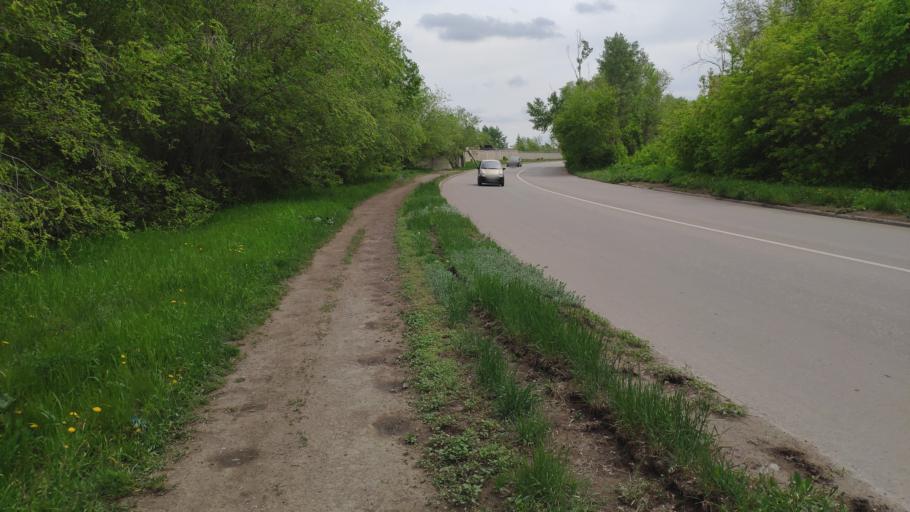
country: RU
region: Chelyabinsk
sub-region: Gorod Magnitogorsk
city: Magnitogorsk
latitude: 53.4158
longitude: 58.9559
